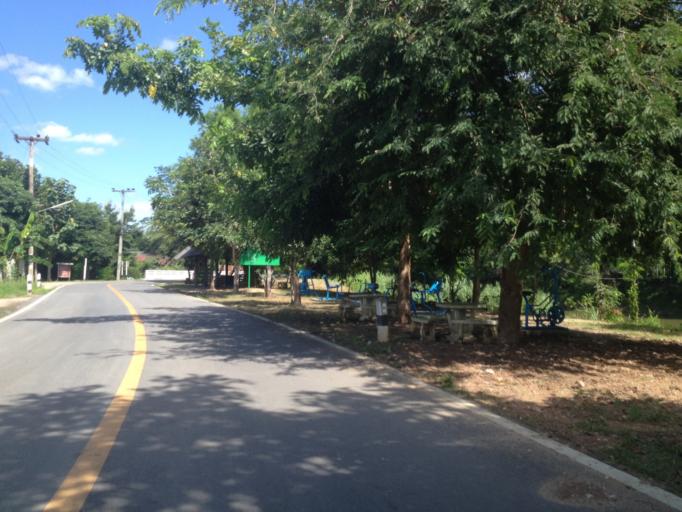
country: TH
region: Chiang Mai
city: Hang Dong
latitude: 18.6772
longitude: 98.9755
